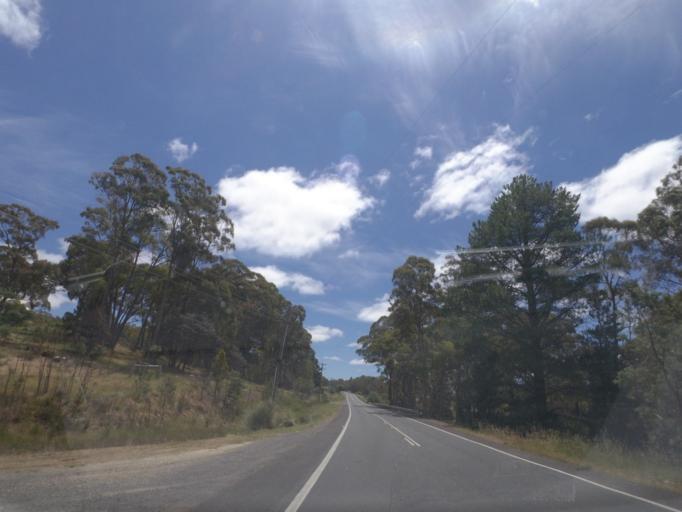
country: AU
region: Victoria
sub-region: Mount Alexander
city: Castlemaine
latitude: -37.2886
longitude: 144.1629
